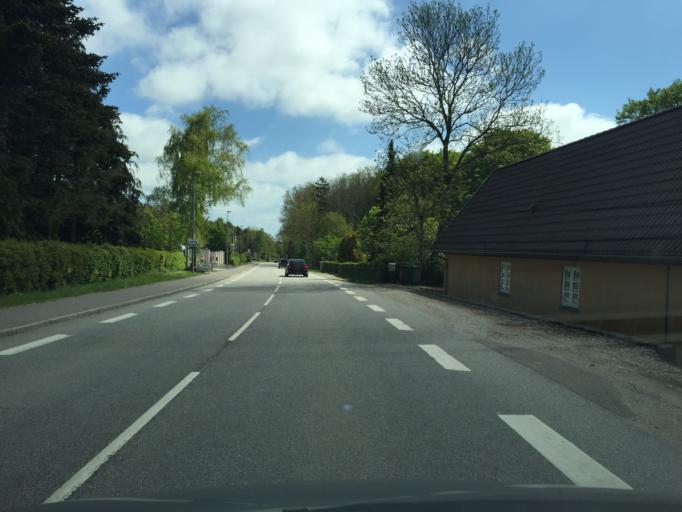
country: DK
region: Zealand
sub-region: Vordingborg Kommune
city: Nyrad
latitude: 54.9970
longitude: 12.0096
